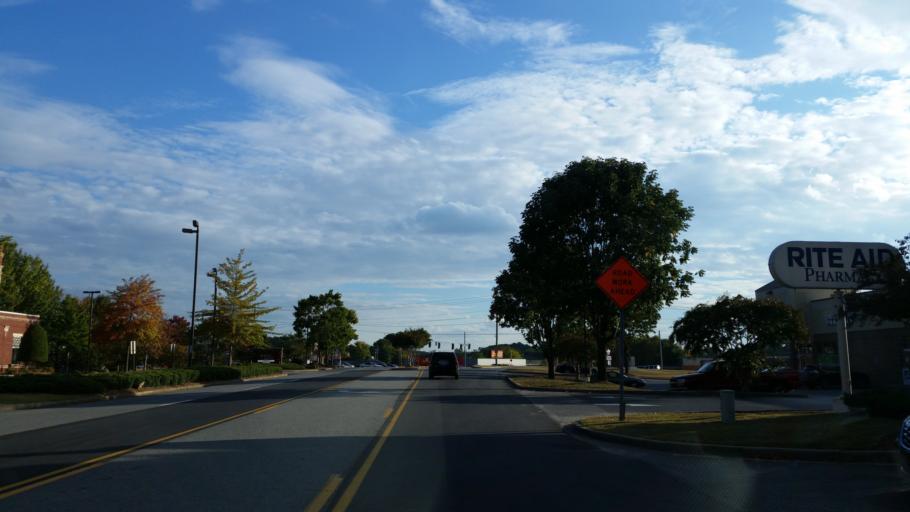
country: US
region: Georgia
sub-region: Bartow County
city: Cartersville
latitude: 34.1999
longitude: -84.7922
